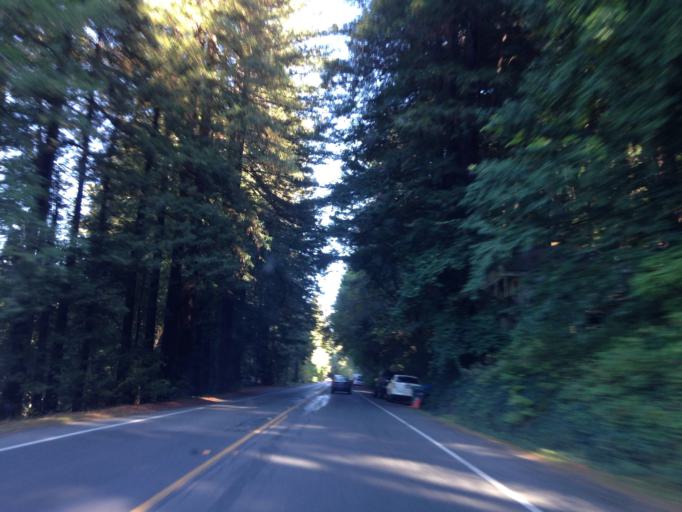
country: US
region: California
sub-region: Sonoma County
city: Monte Rio
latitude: 38.4822
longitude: -123.0096
